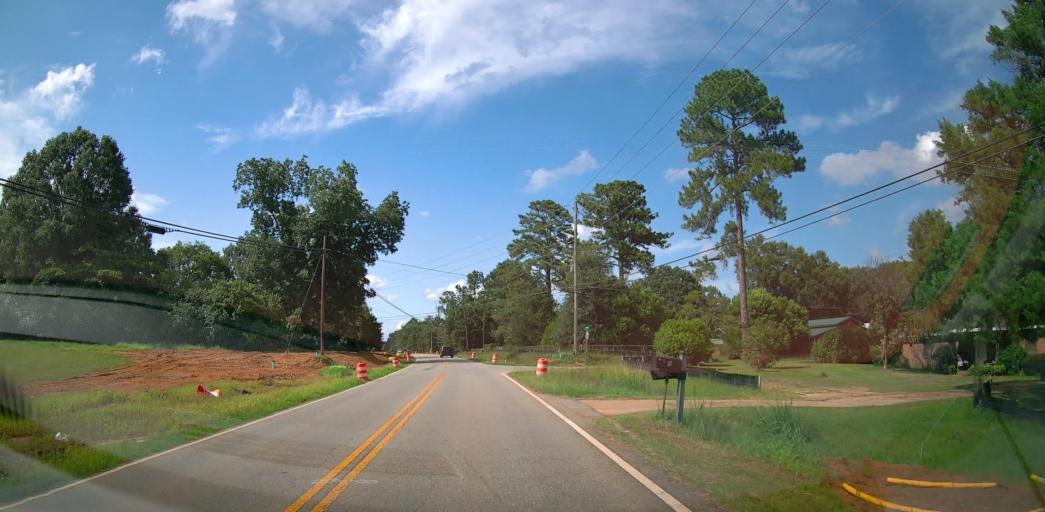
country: US
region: Georgia
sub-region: Houston County
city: Perry
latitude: 32.4823
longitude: -83.7018
